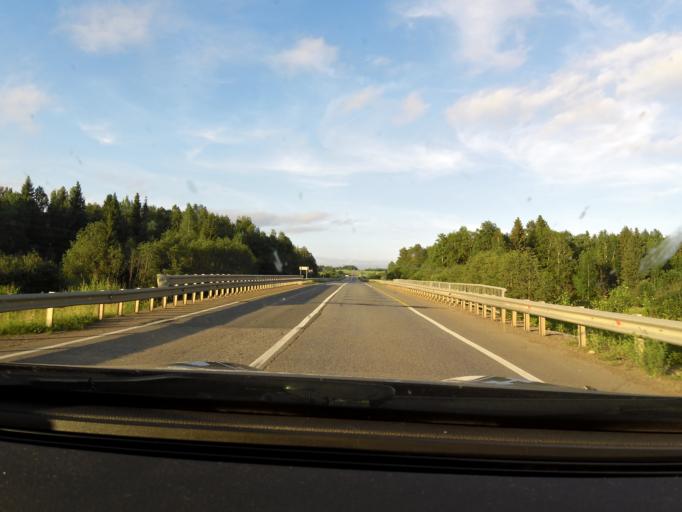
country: RU
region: Perm
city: Siva
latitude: 58.4855
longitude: 54.0842
